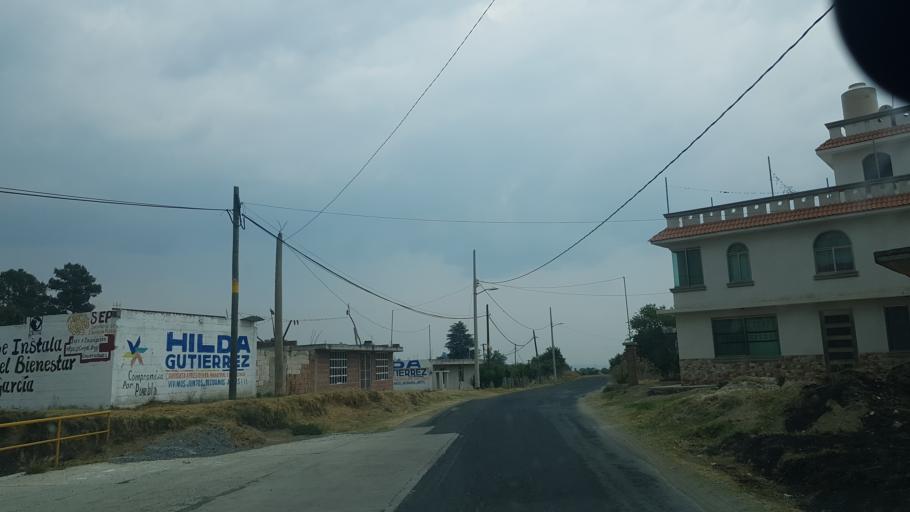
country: MX
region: Puebla
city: San Lorenzo Chiautzingo
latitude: 19.1951
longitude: -98.4655
